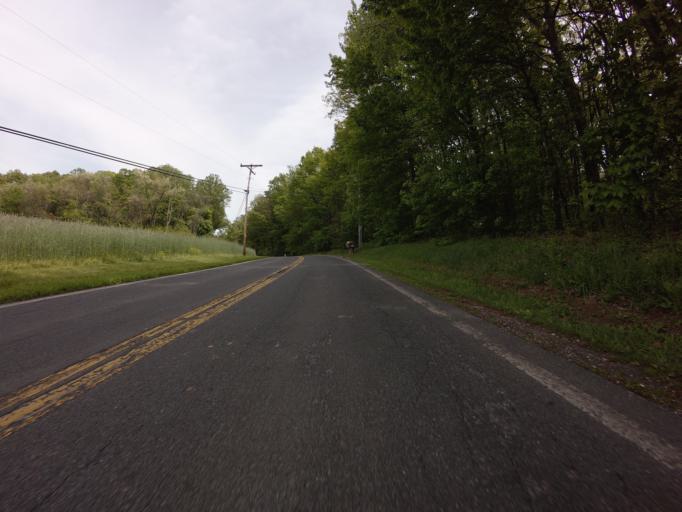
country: US
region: Maryland
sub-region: Carroll County
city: New Windsor
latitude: 39.4613
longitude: -77.0645
